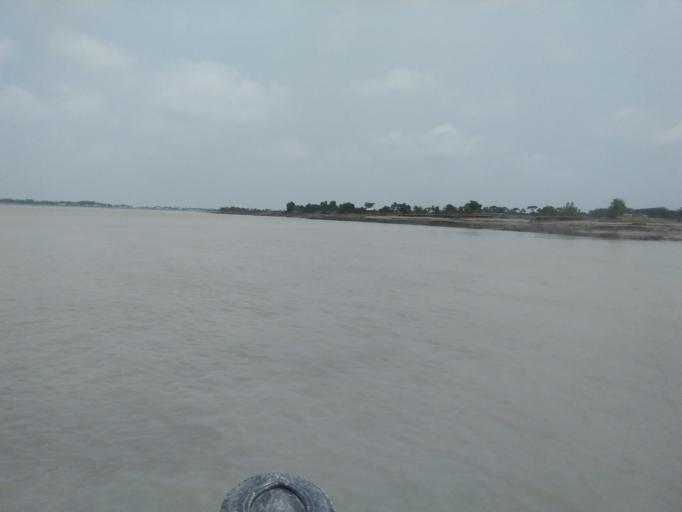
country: BD
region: Khulna
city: Phultala
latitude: 22.6447
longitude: 89.4111
